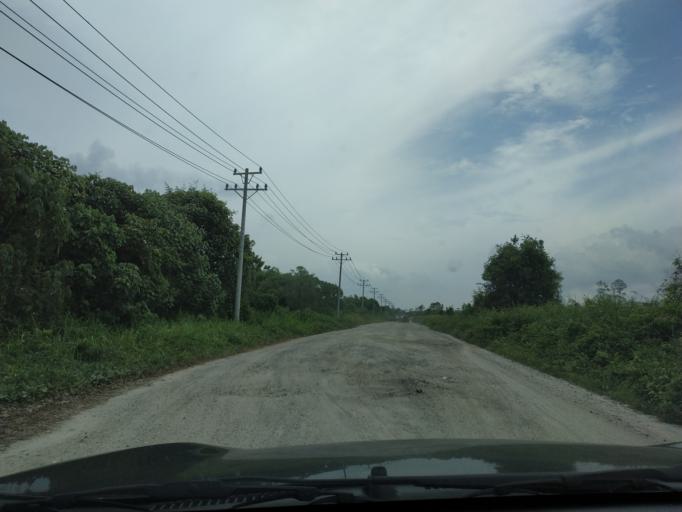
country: ID
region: Riau
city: Siak Sri Indrapura
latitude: 0.9123
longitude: 102.3034
